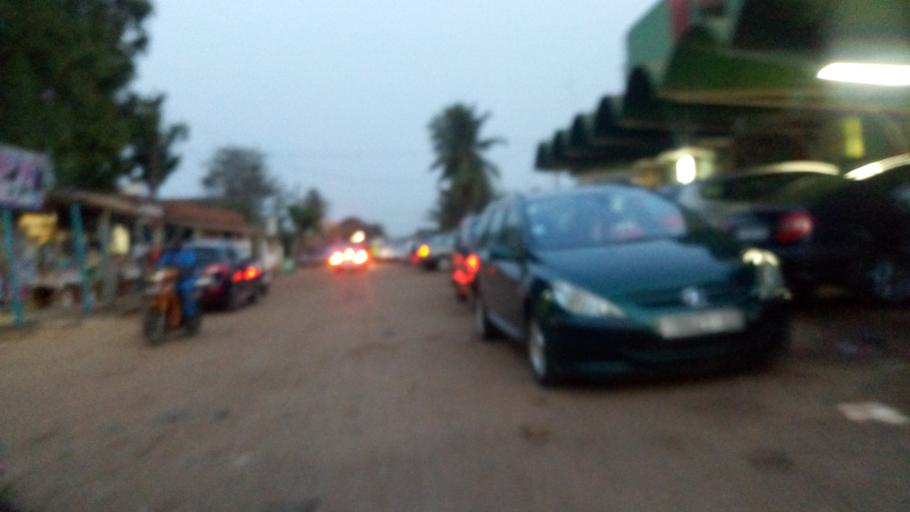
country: TG
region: Maritime
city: Lome
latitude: 6.1676
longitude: 1.2028
